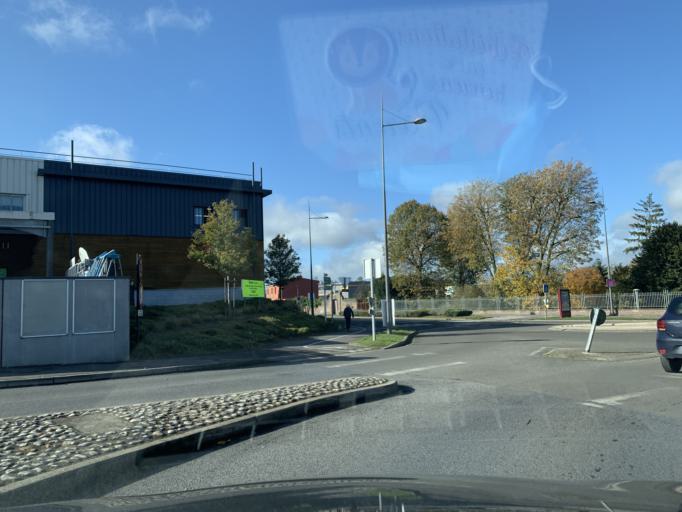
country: FR
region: Nord-Pas-de-Calais
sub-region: Departement du Nord
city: Escaudoeuvres
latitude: 50.1842
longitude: 3.2536
